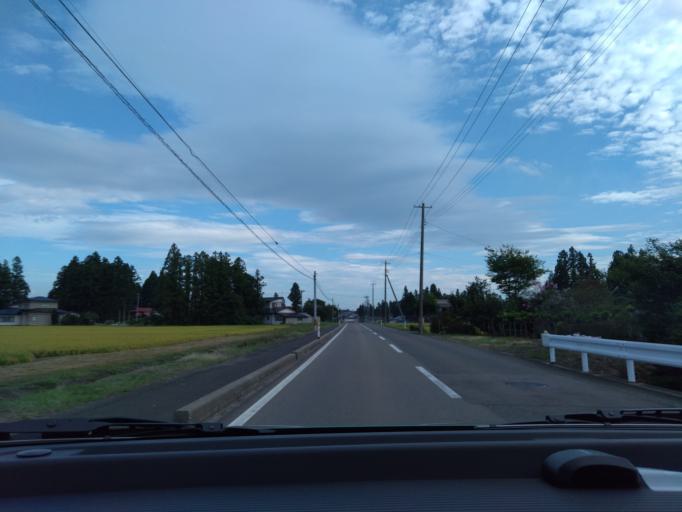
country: JP
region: Iwate
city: Kitakami
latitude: 39.3326
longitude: 141.0542
